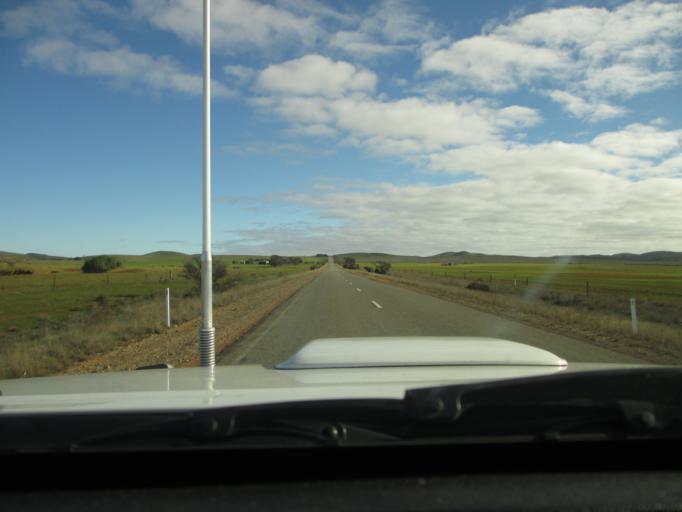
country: AU
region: South Australia
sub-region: Peterborough
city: Peterborough
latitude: -32.6320
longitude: 138.5923
